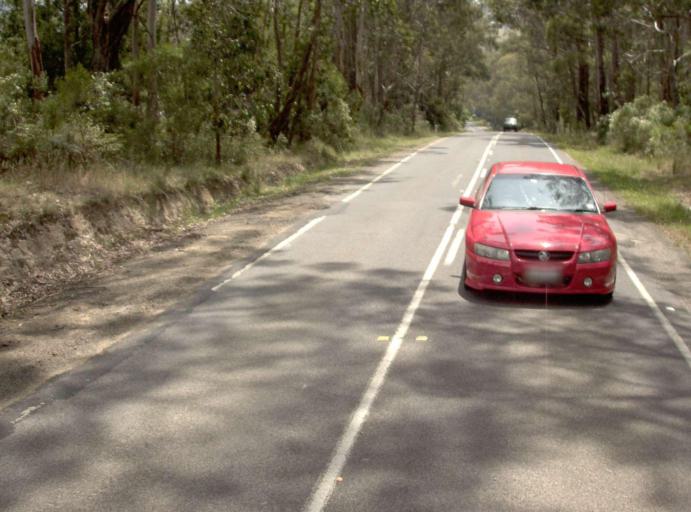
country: AU
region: Victoria
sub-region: Latrobe
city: Traralgon
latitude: -38.3985
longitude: 146.7490
